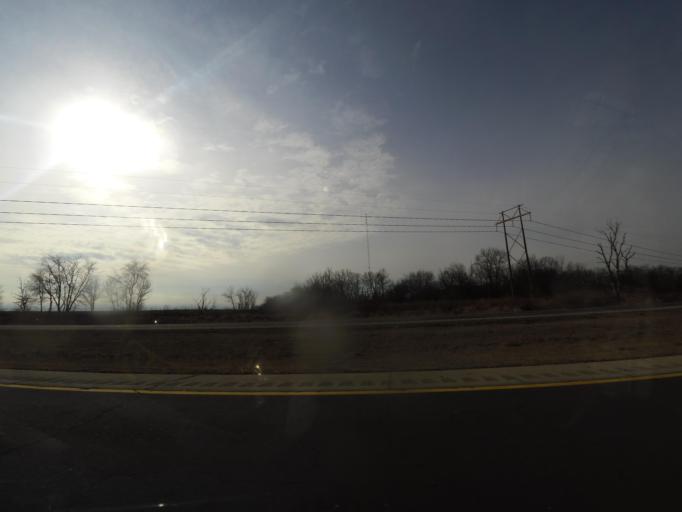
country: US
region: Illinois
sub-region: Macon County
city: Decatur
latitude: 39.7892
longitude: -88.9893
